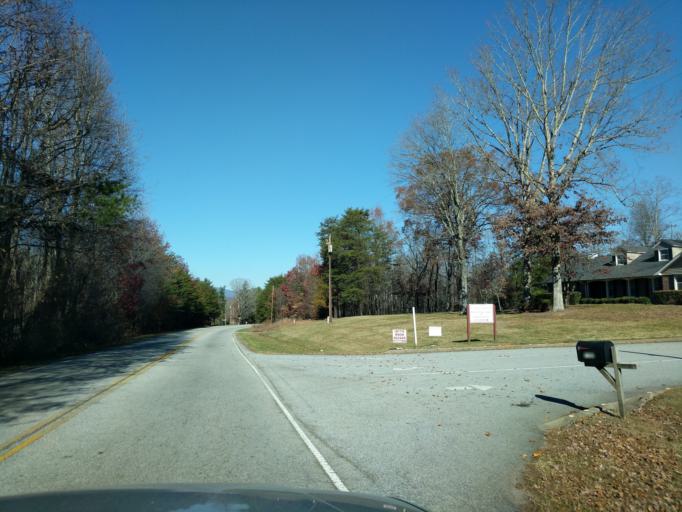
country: US
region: South Carolina
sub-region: Spartanburg County
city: Landrum
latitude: 35.1172
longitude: -82.2249
